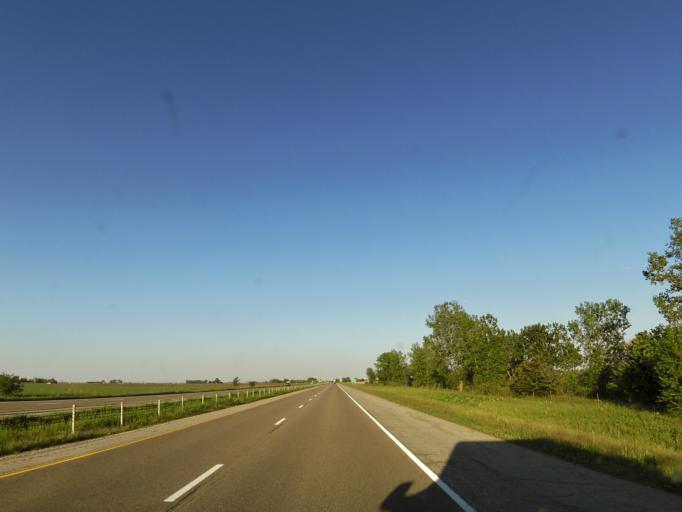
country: US
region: Illinois
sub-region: Champaign County
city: Saint Joseph
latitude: 40.1197
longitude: -87.9810
